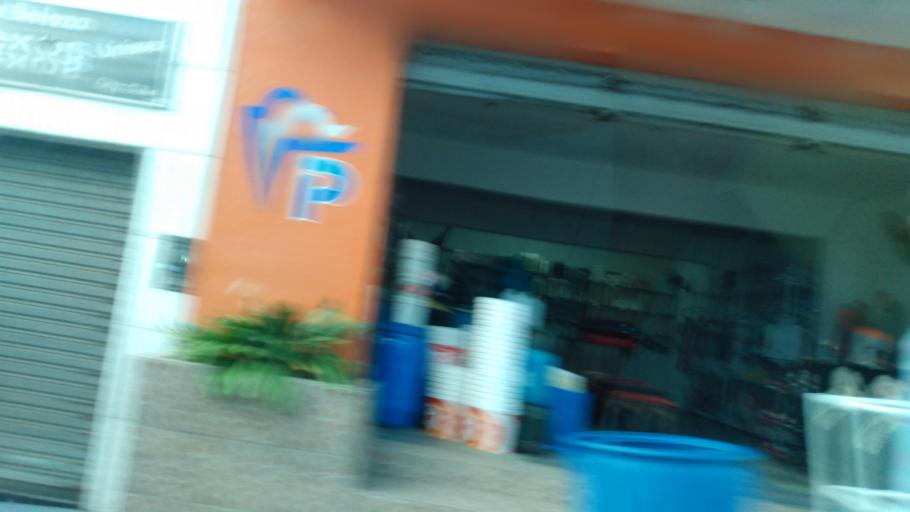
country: BR
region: Pernambuco
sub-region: Bezerros
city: Bezerros
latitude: -8.2351
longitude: -35.7516
